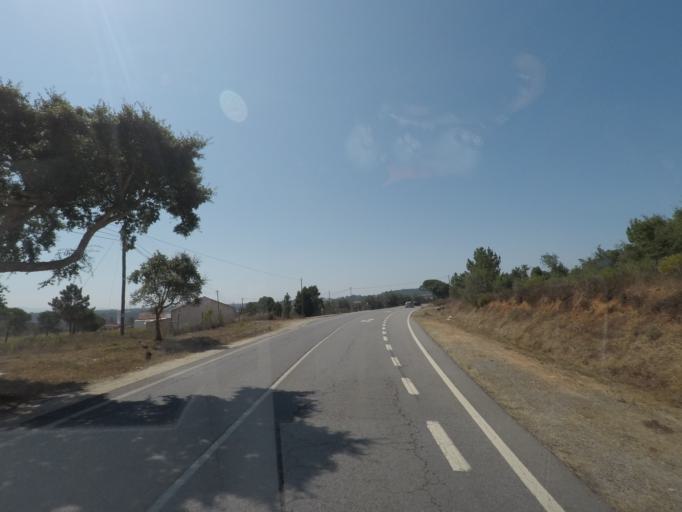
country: PT
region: Beja
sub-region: Odemira
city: Sao Teotonio
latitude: 37.5221
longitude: -8.7012
